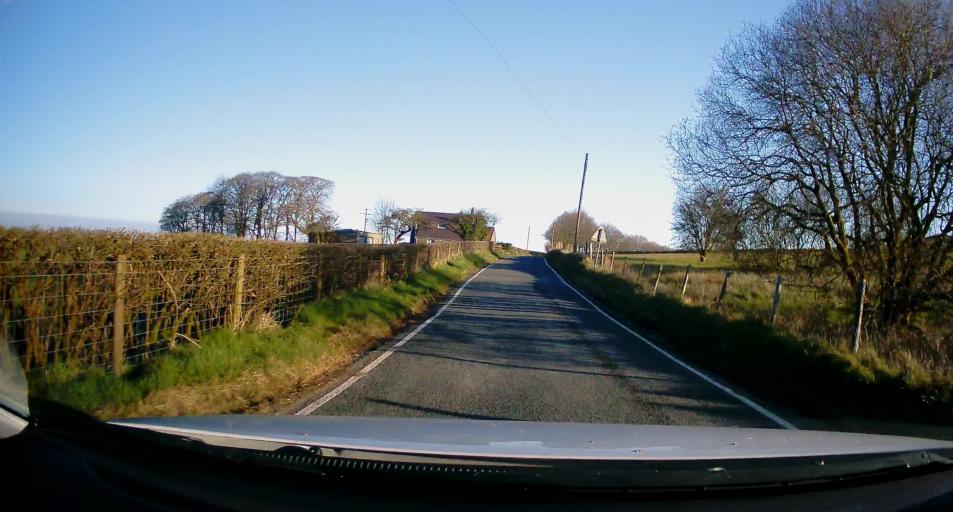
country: GB
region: Wales
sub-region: County of Ceredigion
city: Lledrod
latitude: 52.2640
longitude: -4.0715
